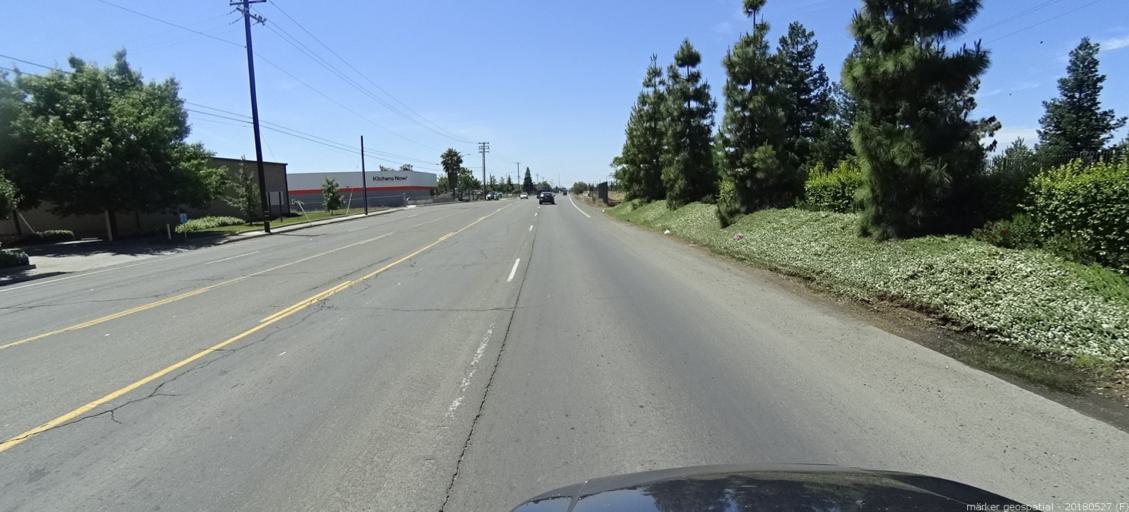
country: US
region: California
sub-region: Sacramento County
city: Florin
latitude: 38.5182
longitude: -121.3907
